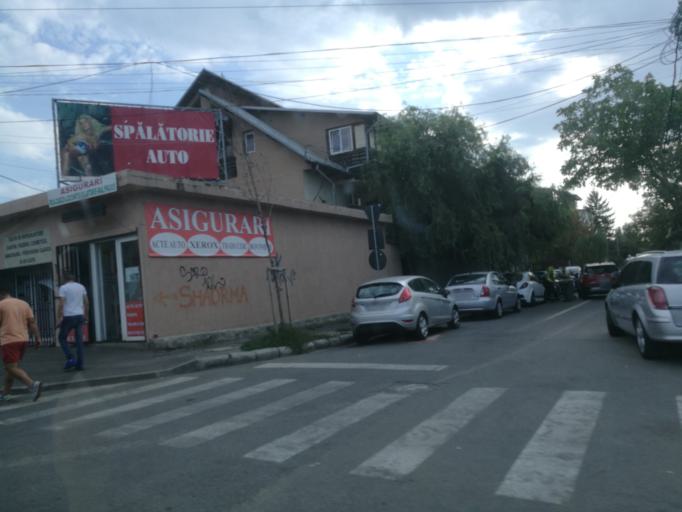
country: RO
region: Ilfov
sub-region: Comuna Chiajna
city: Rosu
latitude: 44.4932
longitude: 26.0327
